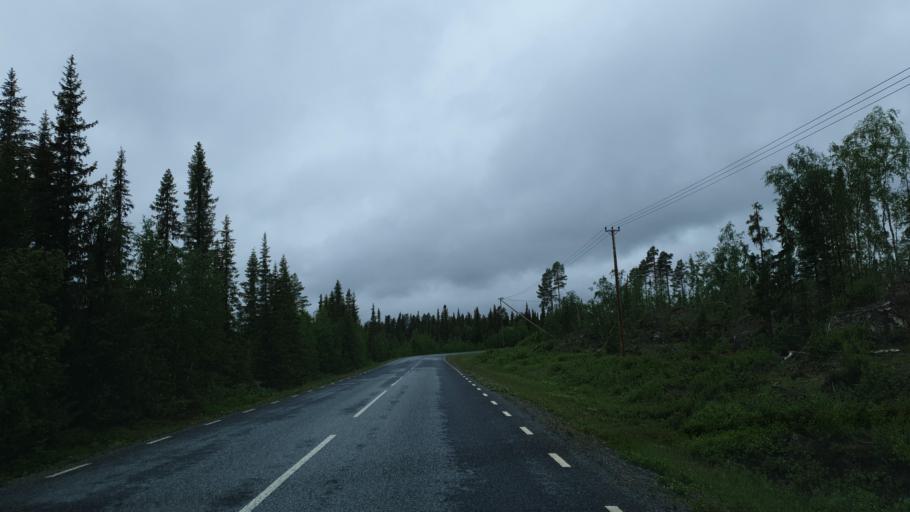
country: SE
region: Vaesterbotten
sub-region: Vilhelmina Kommun
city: Sjoberg
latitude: 65.2347
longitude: 15.8424
